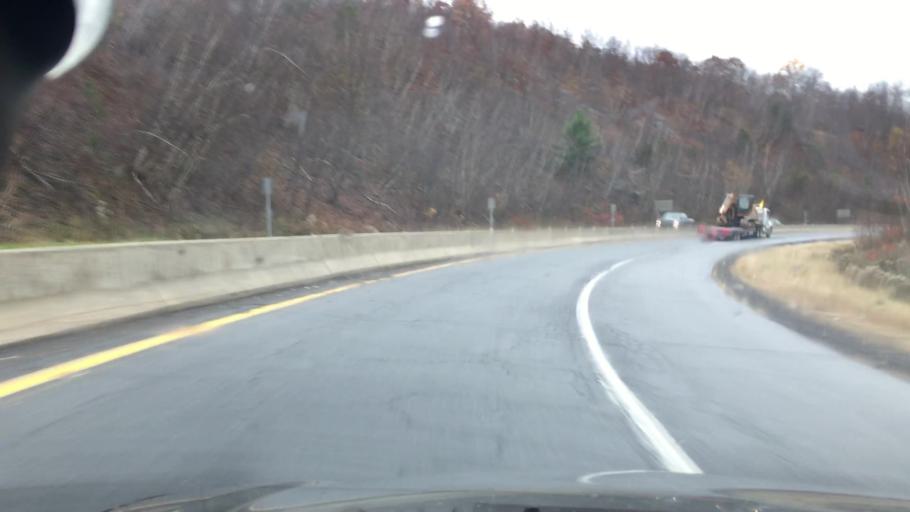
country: US
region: Pennsylvania
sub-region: Luzerne County
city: Ashley
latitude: 41.2028
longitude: -75.9017
